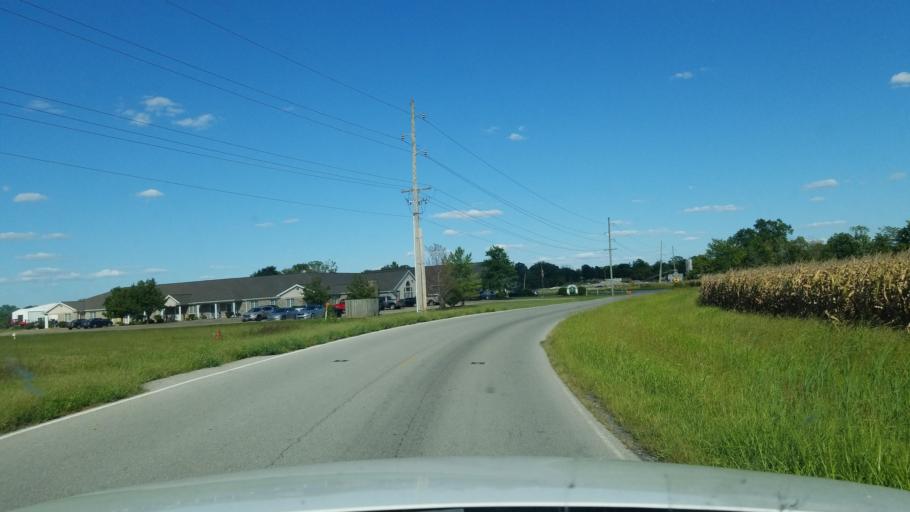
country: US
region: Illinois
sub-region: Saline County
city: Harrisburg
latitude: 37.7202
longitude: -88.5391
